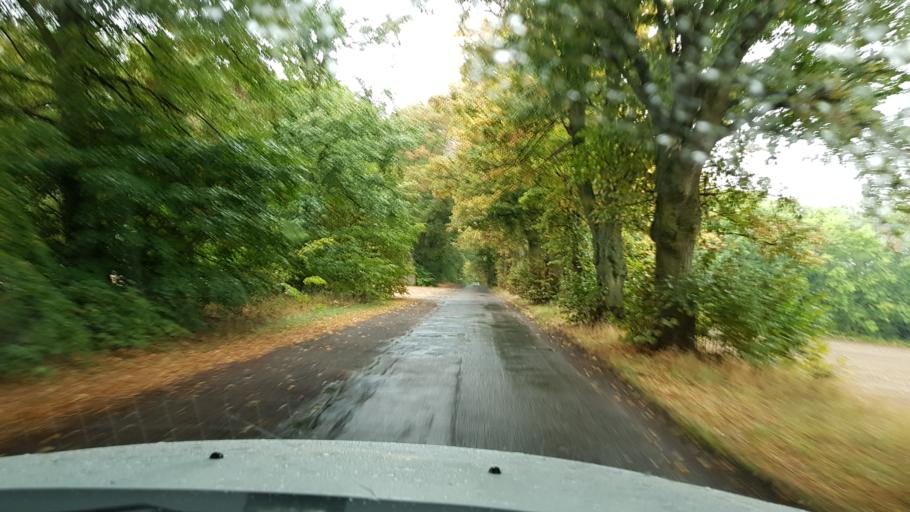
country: DE
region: Brandenburg
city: Schwedt (Oder)
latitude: 53.0059
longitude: 14.2931
